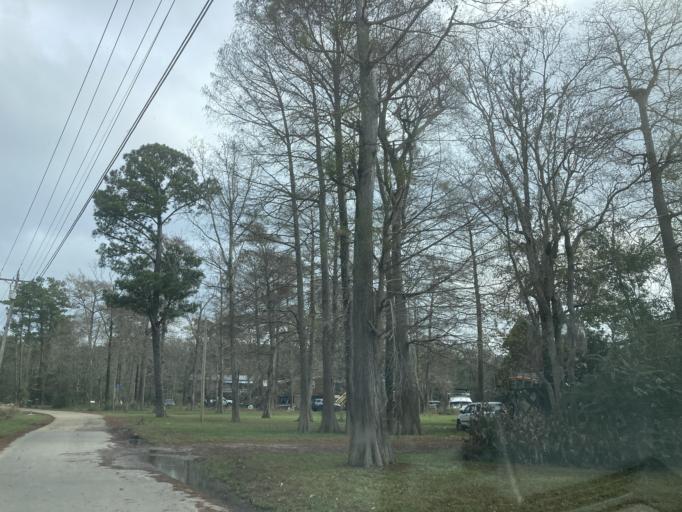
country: US
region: Mississippi
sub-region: Harrison County
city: West Gulfport
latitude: 30.4758
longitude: -89.0181
